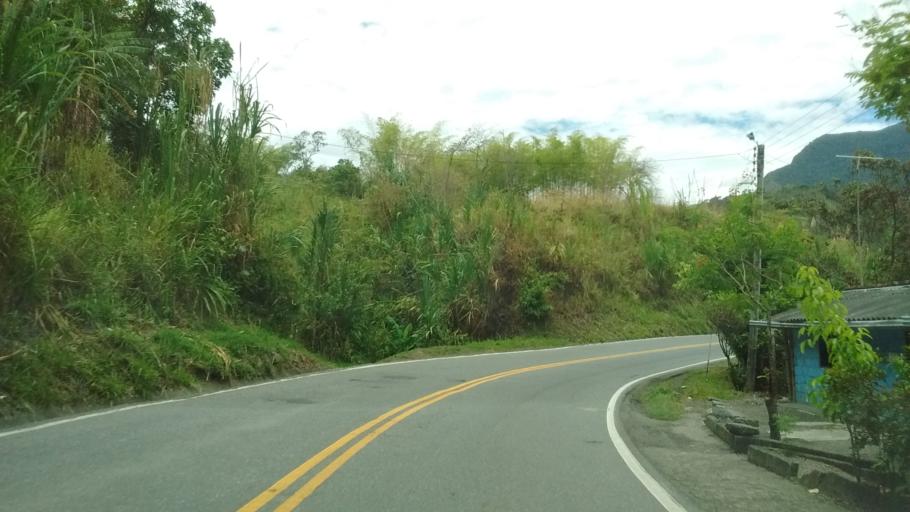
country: CO
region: Cauca
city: Rosas
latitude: 2.2343
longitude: -76.7866
